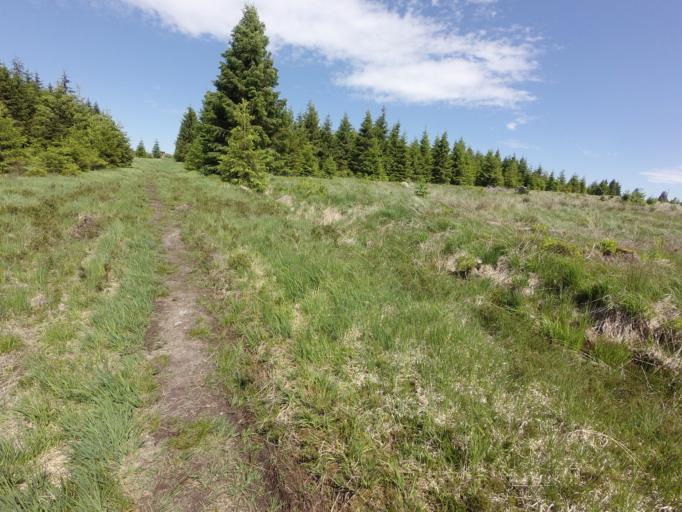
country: BE
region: Wallonia
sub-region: Province de Liege
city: Malmedy
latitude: 50.5117
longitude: 6.0393
